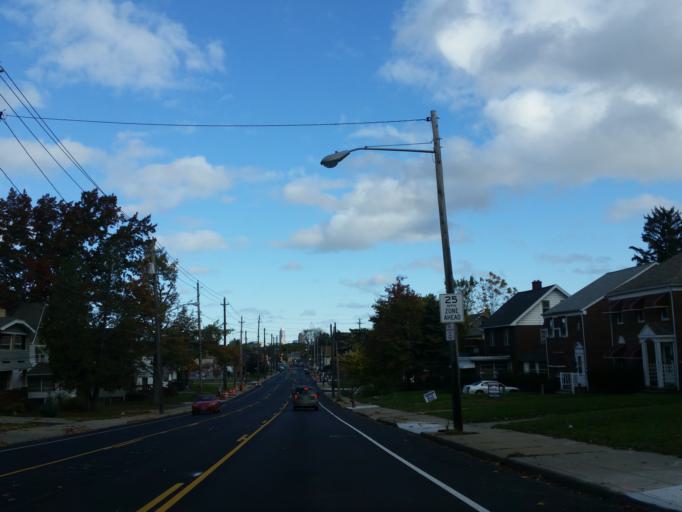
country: US
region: Ohio
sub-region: Cuyahoga County
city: Brooklyn Heights
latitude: 41.4310
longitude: -81.6973
